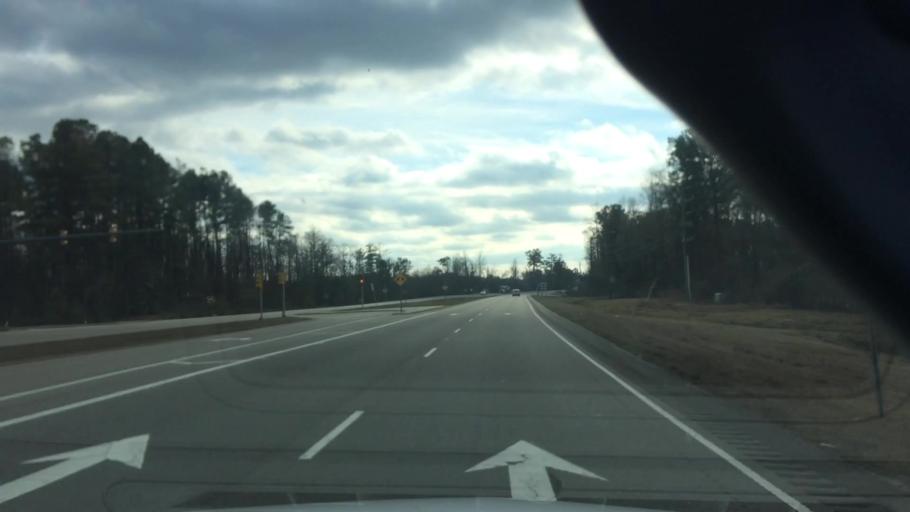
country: US
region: North Carolina
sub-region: Brunswick County
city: Bolivia
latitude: 34.1376
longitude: -78.0937
